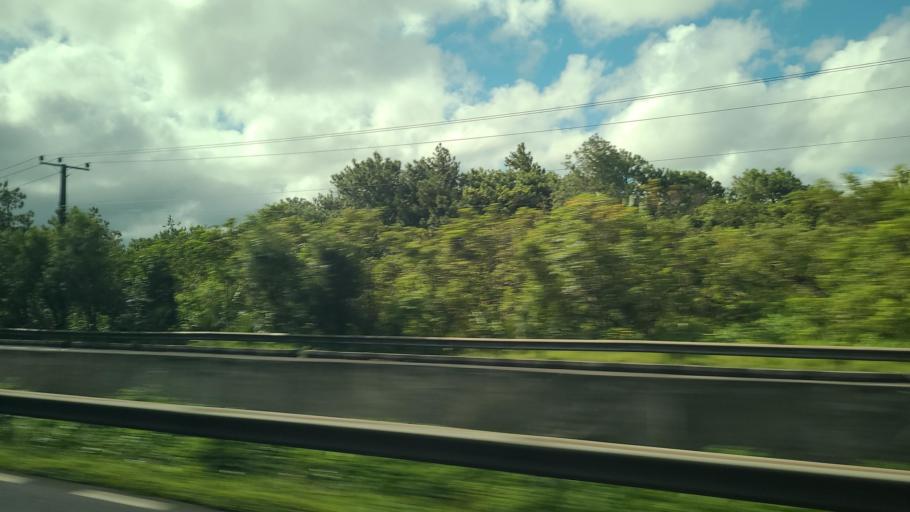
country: MU
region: Plaines Wilhems
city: Midlands
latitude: -20.3304
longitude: 57.5509
